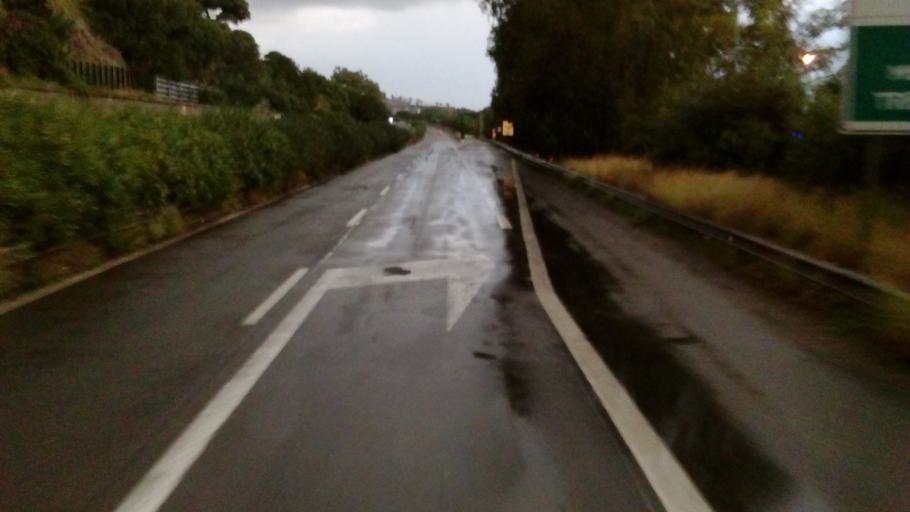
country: IT
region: Sicily
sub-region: Messina
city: Larderia
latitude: 38.1291
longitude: 15.5190
